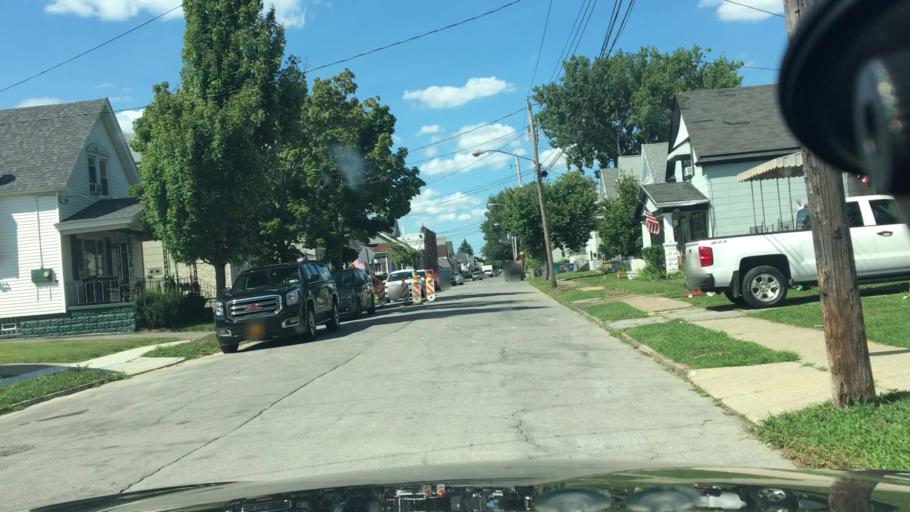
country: US
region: New York
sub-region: Erie County
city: West Seneca
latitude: 42.8705
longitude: -78.8059
